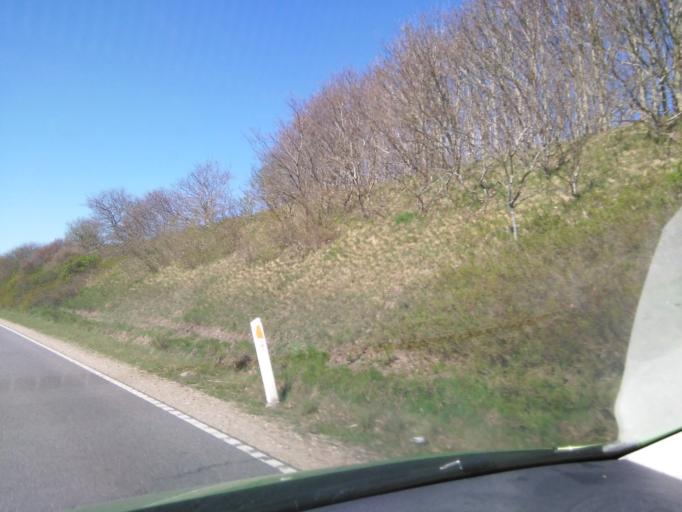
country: DK
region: South Denmark
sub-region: Varde Kommune
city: Oksbol
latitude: 55.6193
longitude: 8.2930
